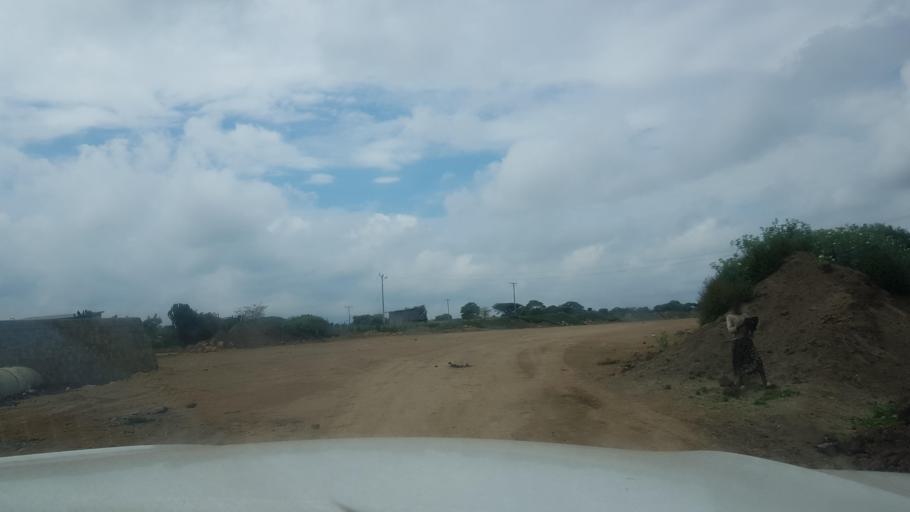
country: ET
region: Oromiya
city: Shashemene
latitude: 7.2557
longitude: 38.5935
